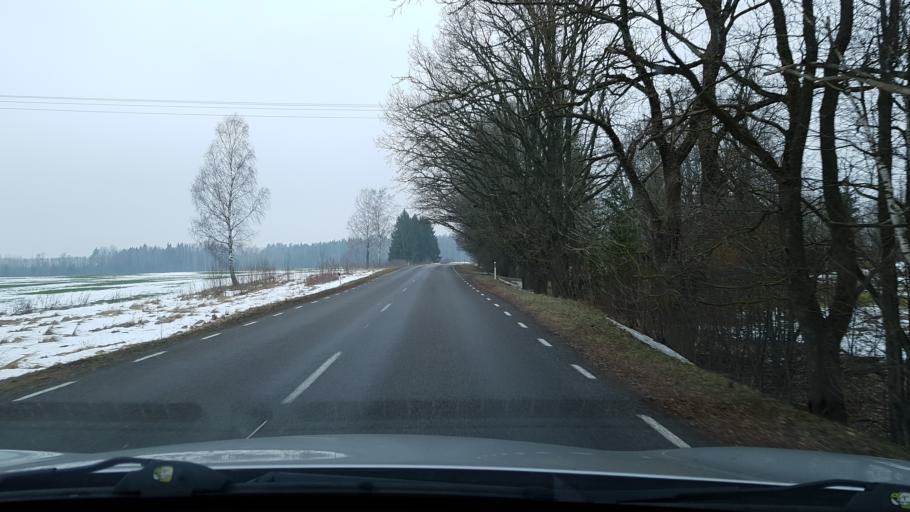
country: EE
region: Valgamaa
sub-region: Torva linn
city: Torva
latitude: 58.0904
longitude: 26.0178
